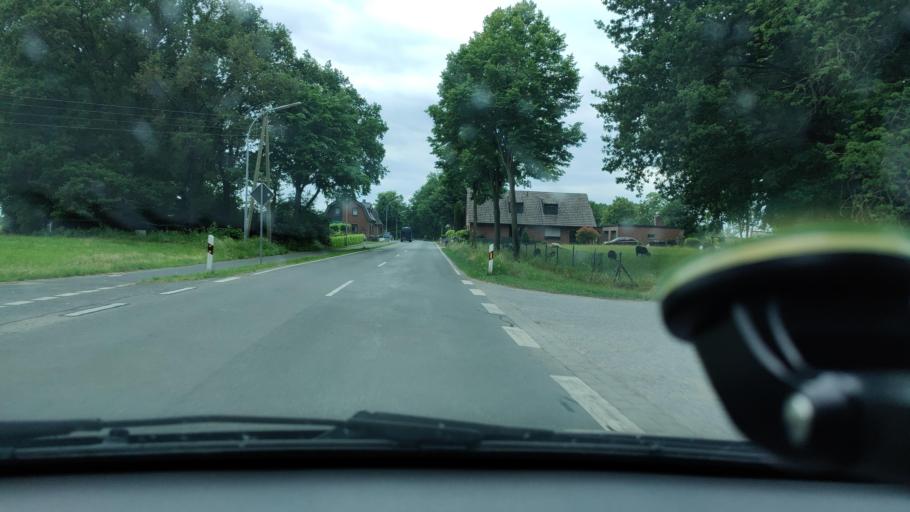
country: NL
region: Limburg
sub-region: Gemeente Gennep
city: Gennep
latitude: 51.6879
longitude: 6.0577
